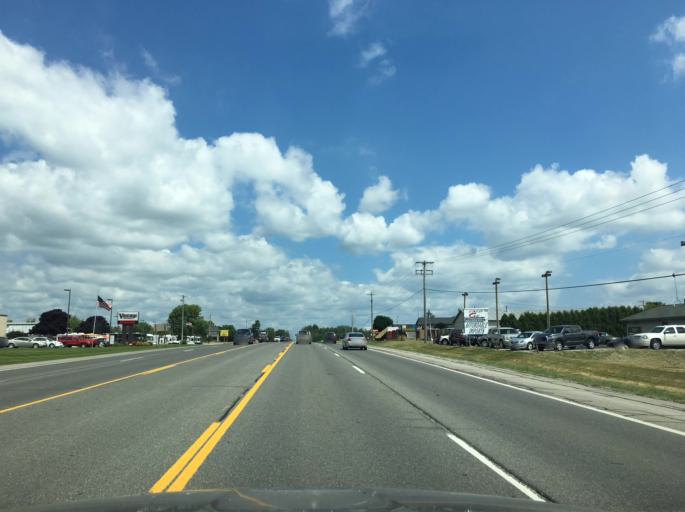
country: US
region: Michigan
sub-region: Grand Traverse County
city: Traverse City
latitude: 44.6952
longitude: -85.6562
